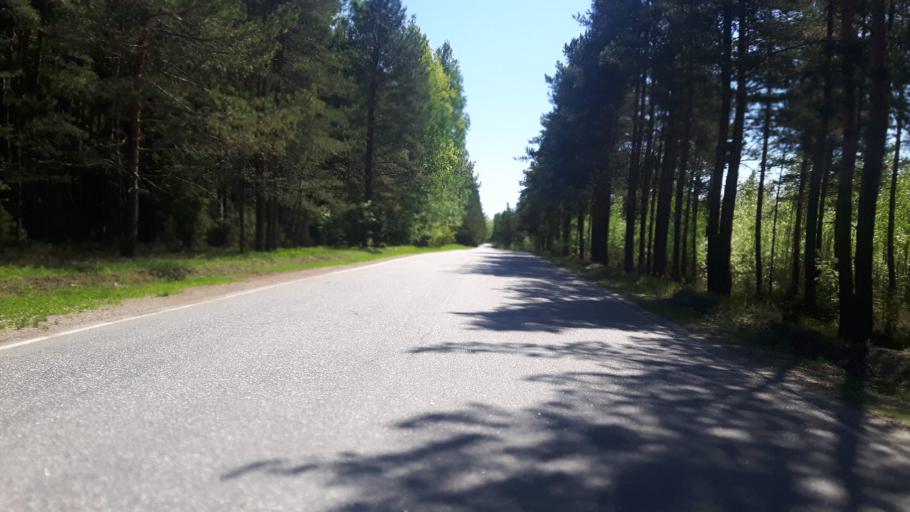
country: RU
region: Leningrad
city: Glebychevo
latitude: 60.3531
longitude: 28.8154
